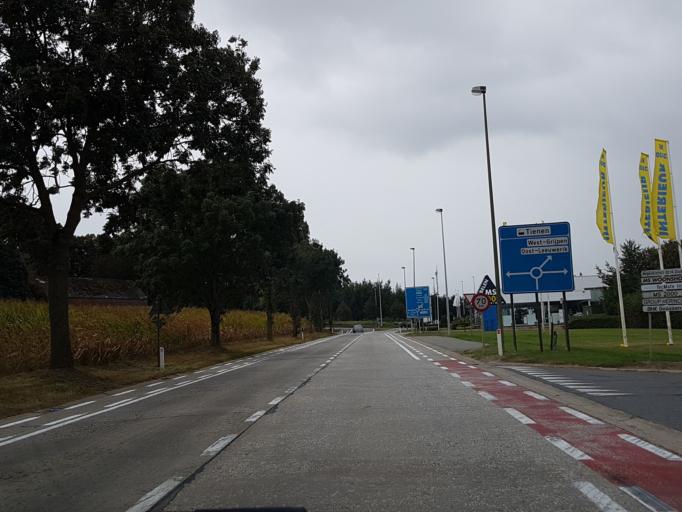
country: BE
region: Flanders
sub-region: Provincie Vlaams-Brabant
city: Tienen
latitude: 50.8008
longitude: 4.9727
